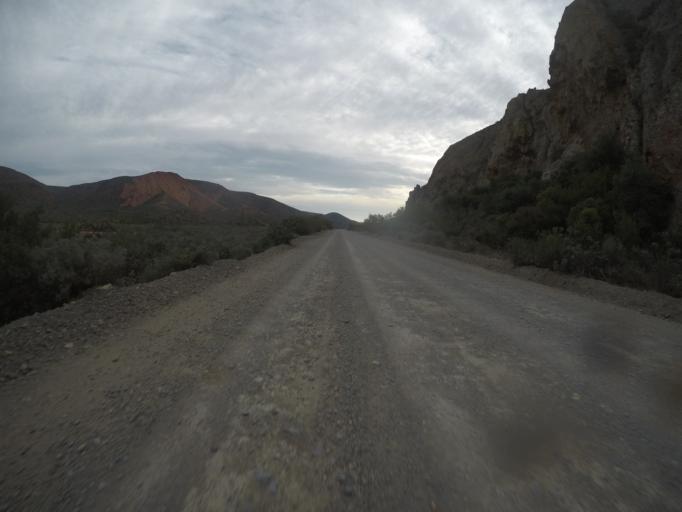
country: ZA
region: Eastern Cape
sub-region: Cacadu District Municipality
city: Willowmore
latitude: -33.5230
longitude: 23.6569
